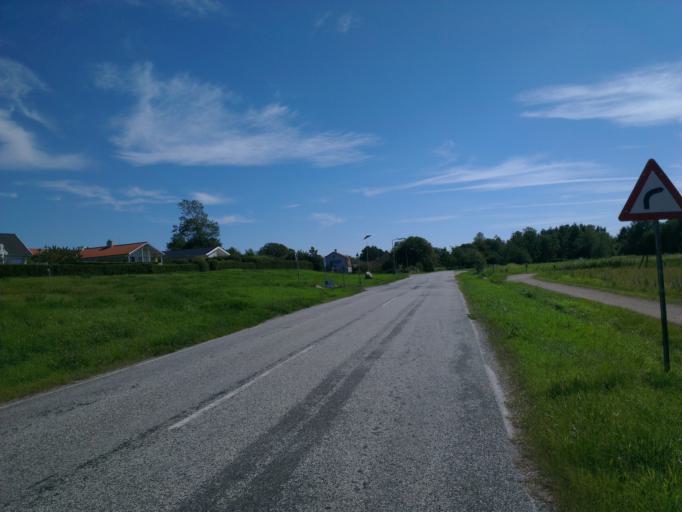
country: DK
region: Capital Region
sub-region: Frederikssund Kommune
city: Frederikssund
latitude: 55.8585
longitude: 12.0704
